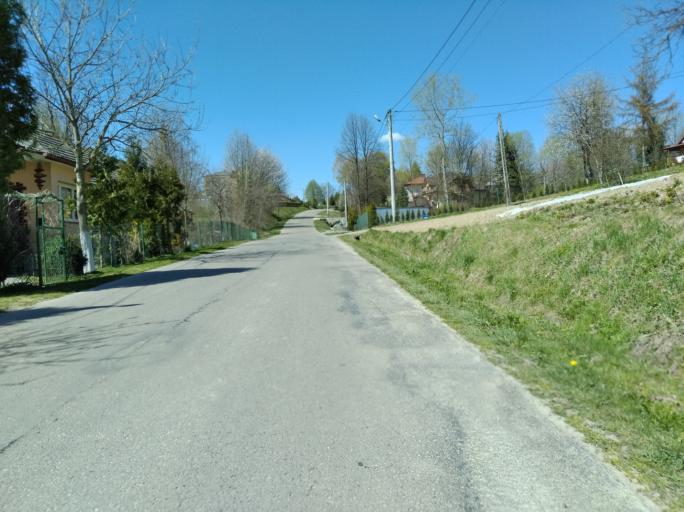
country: PL
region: Subcarpathian Voivodeship
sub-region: Powiat brzozowski
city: Jablonka
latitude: 49.7226
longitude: 22.1178
